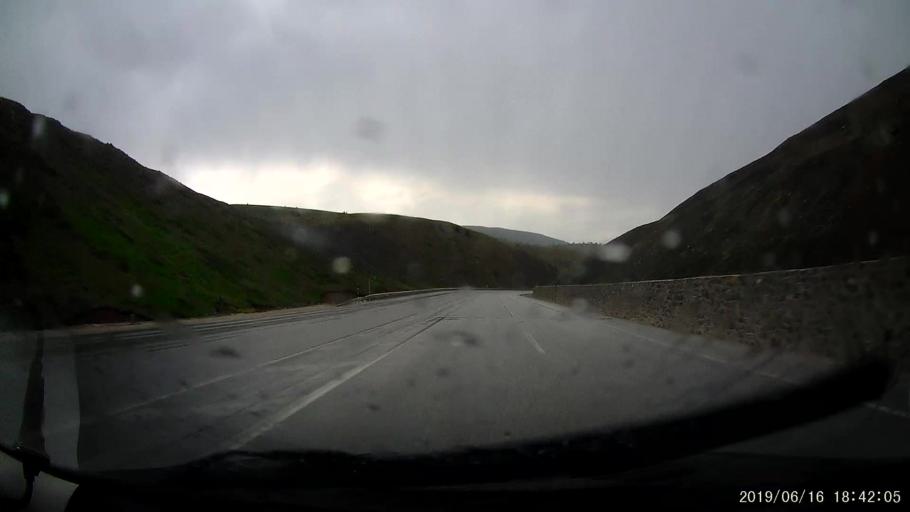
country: TR
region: Erzincan
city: Doganbeyli
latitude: 39.8717
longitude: 39.1163
